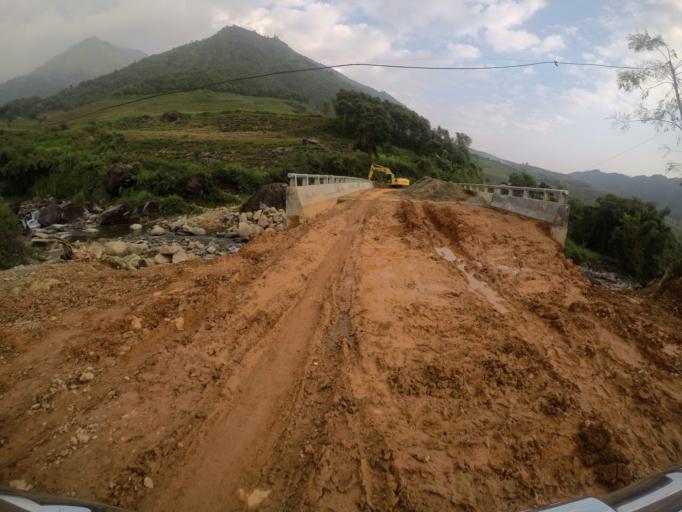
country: VN
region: Lai Chau
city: Than Uyen
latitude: 22.1388
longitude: 103.8183
